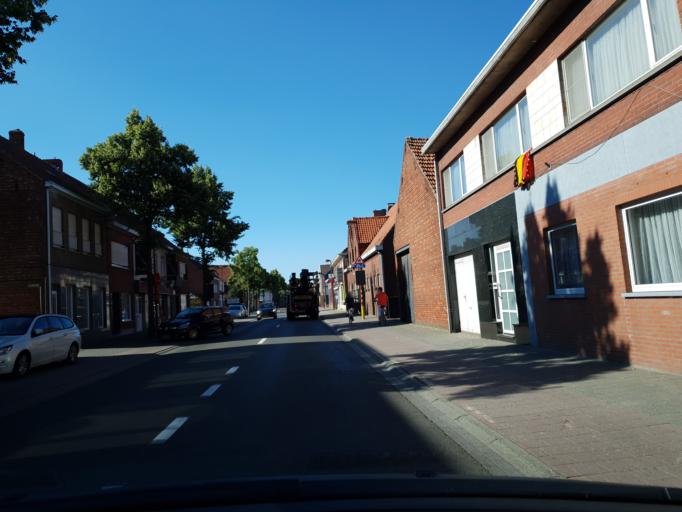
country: BE
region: Flanders
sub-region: Provincie Antwerpen
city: Rijkevorsel
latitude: 51.3511
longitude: 4.7603
